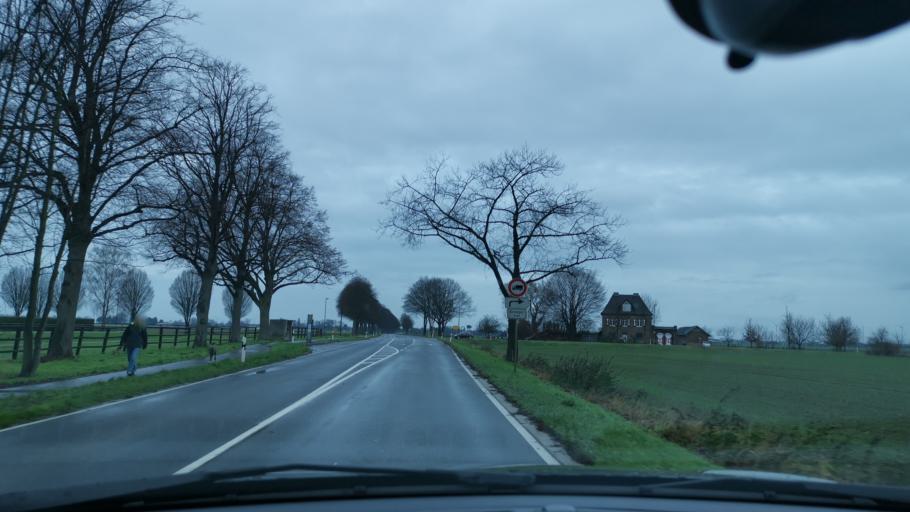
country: DE
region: North Rhine-Westphalia
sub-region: Regierungsbezirk Koln
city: Bedburg
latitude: 50.9887
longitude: 6.5080
